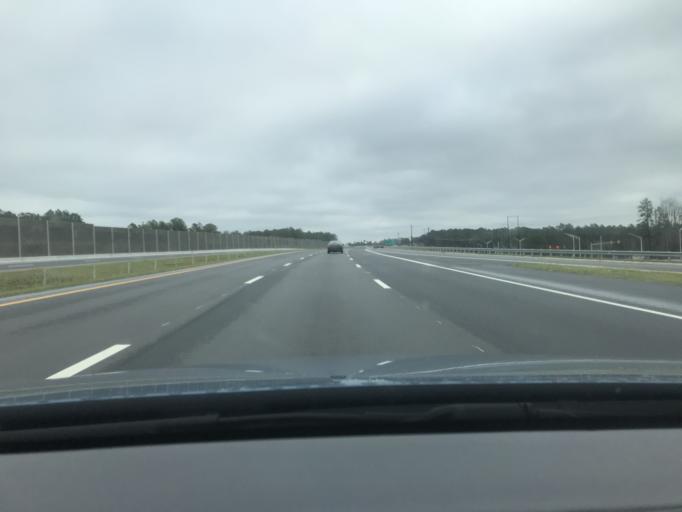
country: US
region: North Carolina
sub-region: Cumberland County
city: Fort Bragg
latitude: 35.1073
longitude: -79.0088
